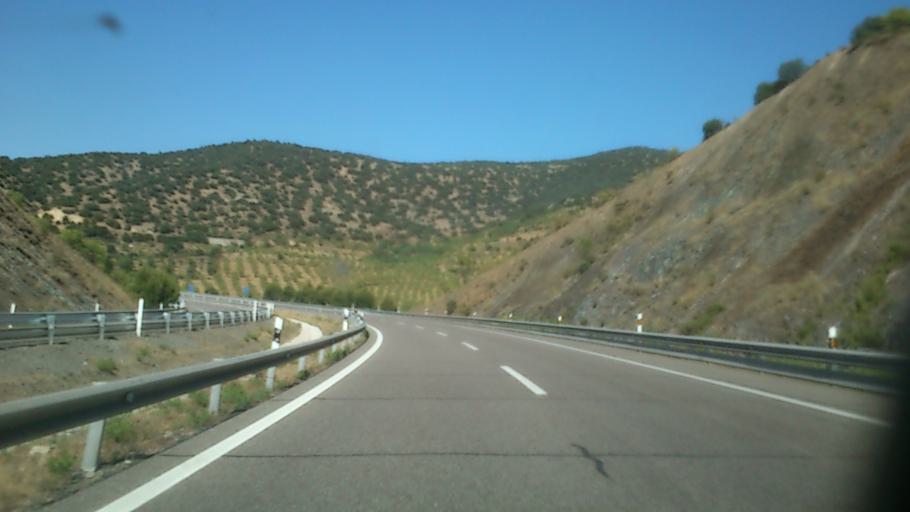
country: ES
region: Aragon
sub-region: Provincia de Zaragoza
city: Paracuellos de la Ribera
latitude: 41.4018
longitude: -1.5300
